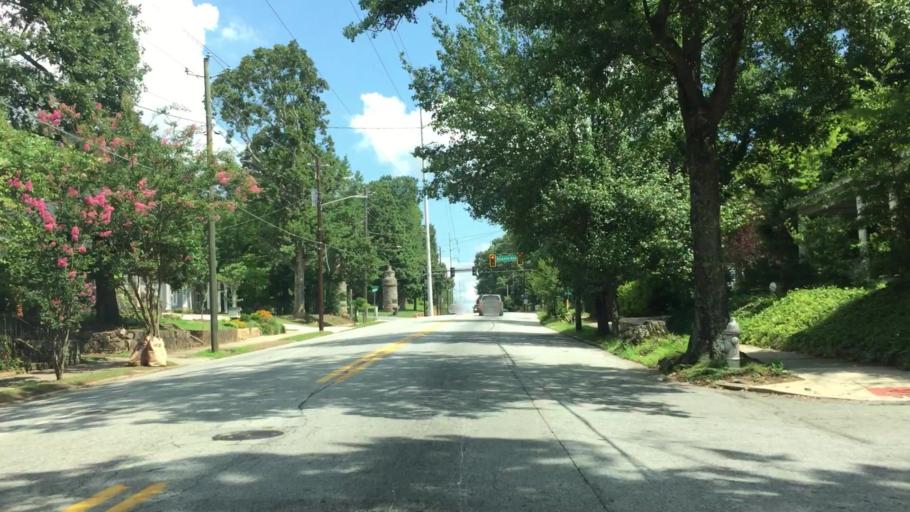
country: US
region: Georgia
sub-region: Fulton County
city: Atlanta
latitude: 33.7293
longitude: -84.3684
